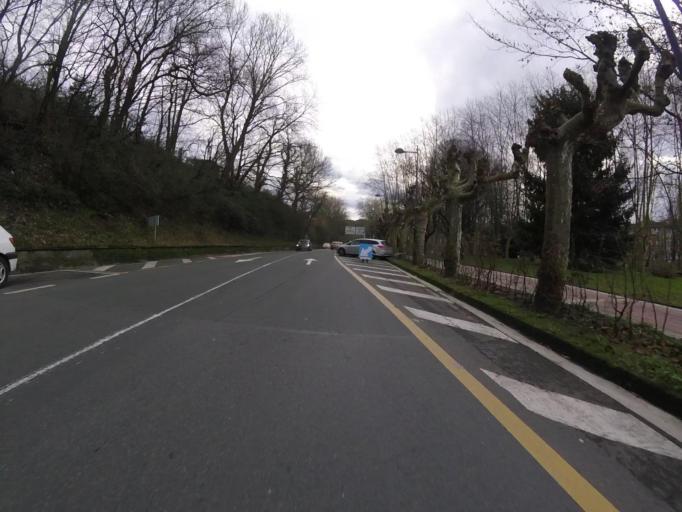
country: ES
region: Basque Country
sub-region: Provincia de Guipuzcoa
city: Errenteria
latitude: 43.3106
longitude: -1.8884
